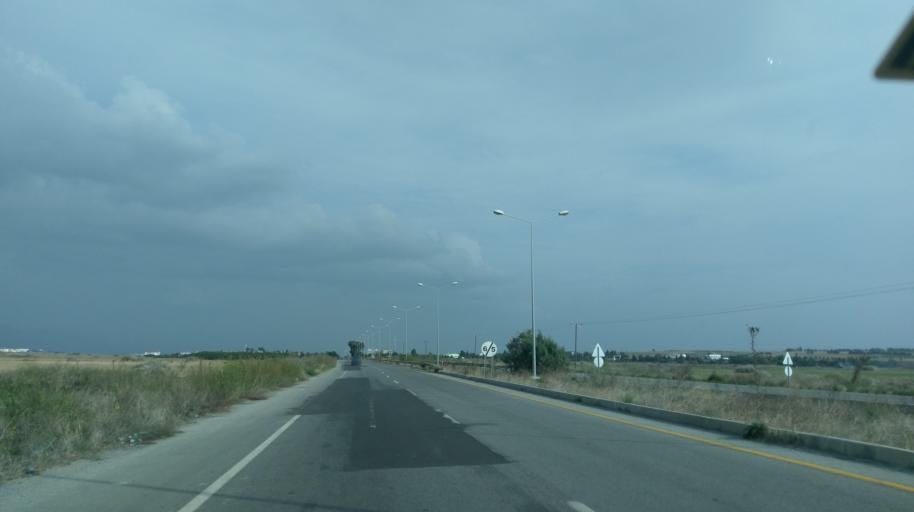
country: CY
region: Lefkosia
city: Mammari
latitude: 35.2110
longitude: 33.2222
